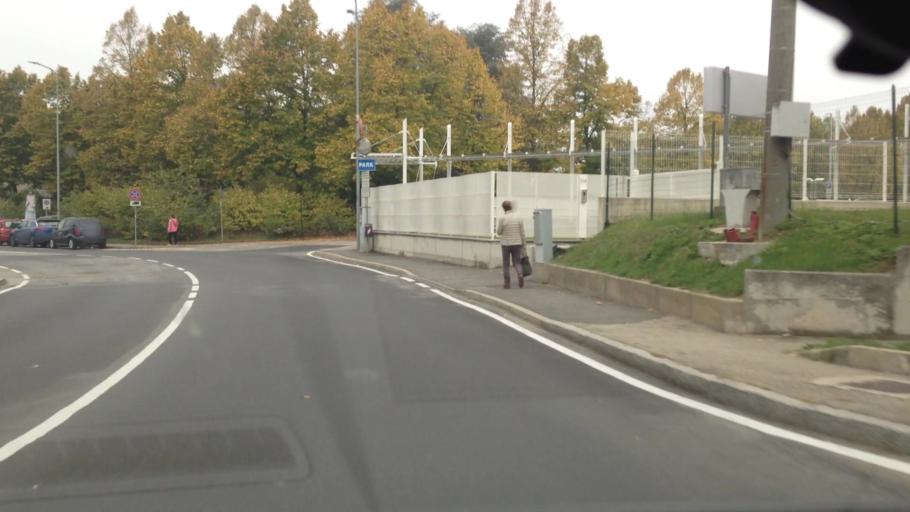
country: IT
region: Piedmont
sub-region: Provincia di Asti
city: Asti
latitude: 44.9105
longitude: 8.1971
